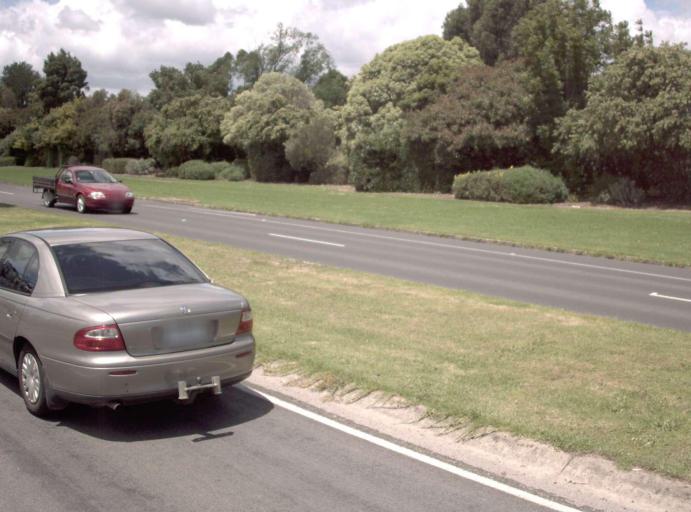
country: AU
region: Victoria
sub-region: Baw Baw
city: Warragul
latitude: -38.1588
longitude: 145.9217
